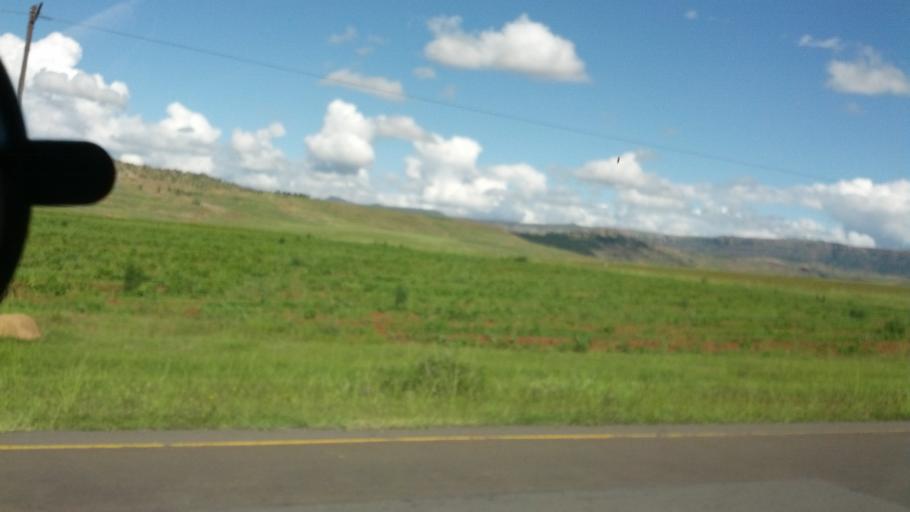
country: LS
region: Maseru
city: Maseru
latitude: -29.5577
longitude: 27.4946
